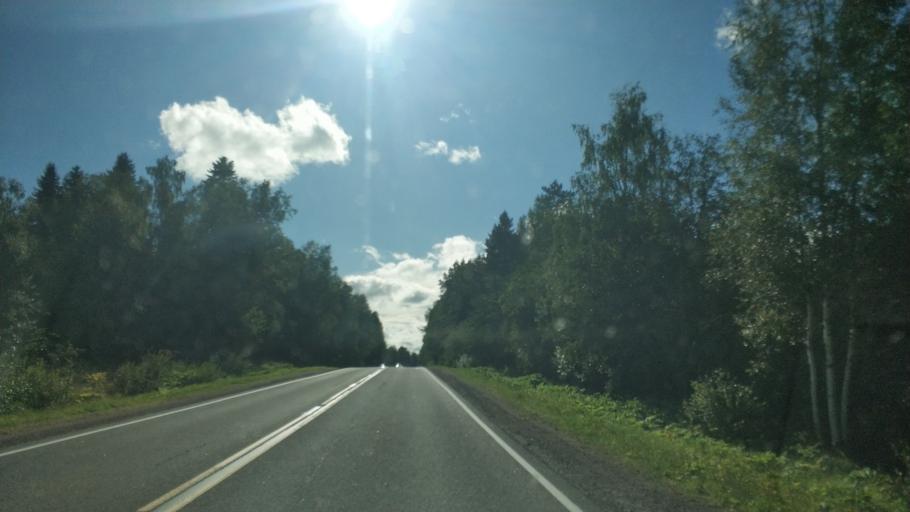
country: RU
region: Republic of Karelia
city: Khelyulya
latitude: 61.6528
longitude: 30.6089
